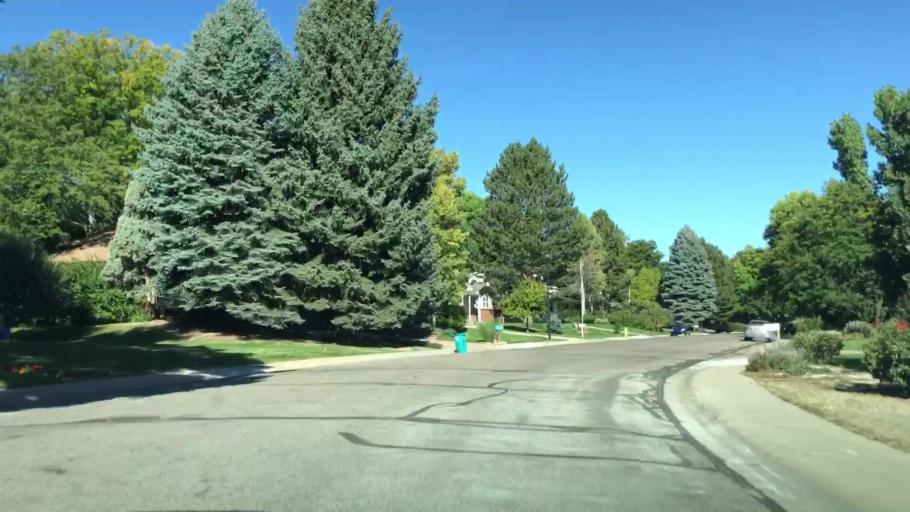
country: US
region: Colorado
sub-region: Larimer County
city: Fort Collins
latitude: 40.5553
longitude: -105.0498
